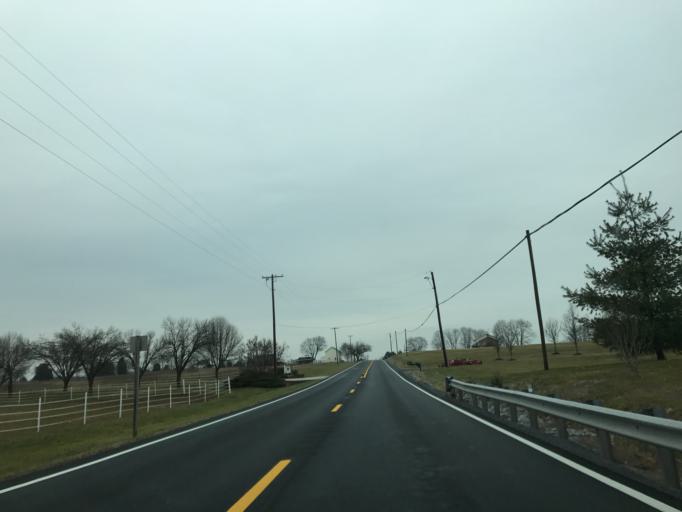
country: US
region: Maryland
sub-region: Frederick County
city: Emmitsburg
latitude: 39.6831
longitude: -77.2507
